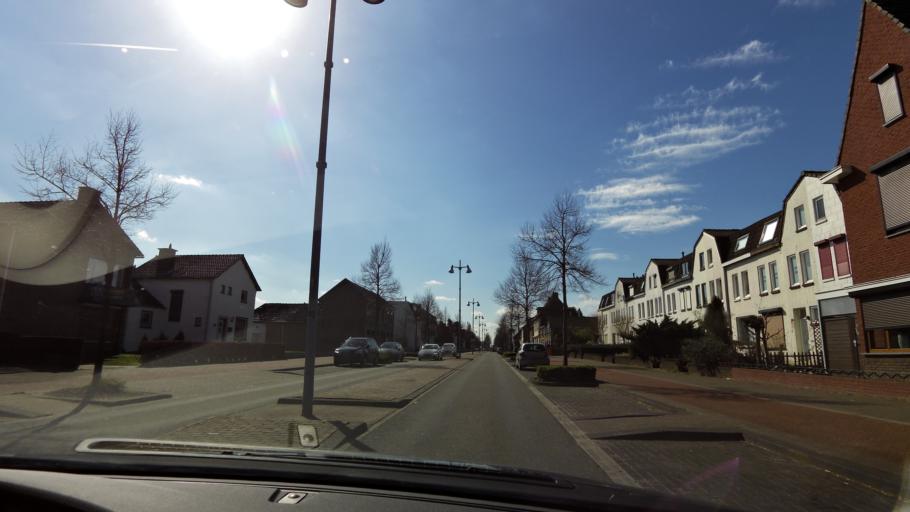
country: NL
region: Limburg
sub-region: Gemeente Beek
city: Beek
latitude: 50.9612
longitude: 5.8201
